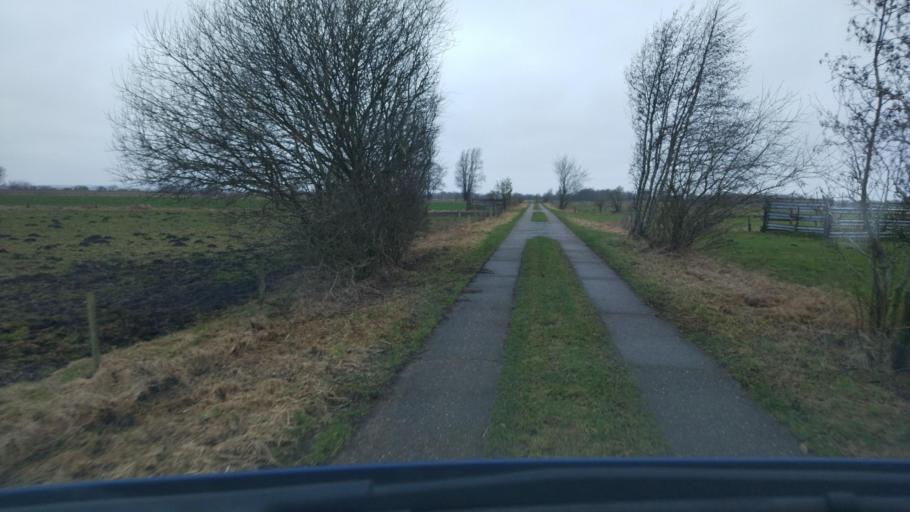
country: DE
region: Schleswig-Holstein
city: Gross Rheide
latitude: 54.4580
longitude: 9.4206
